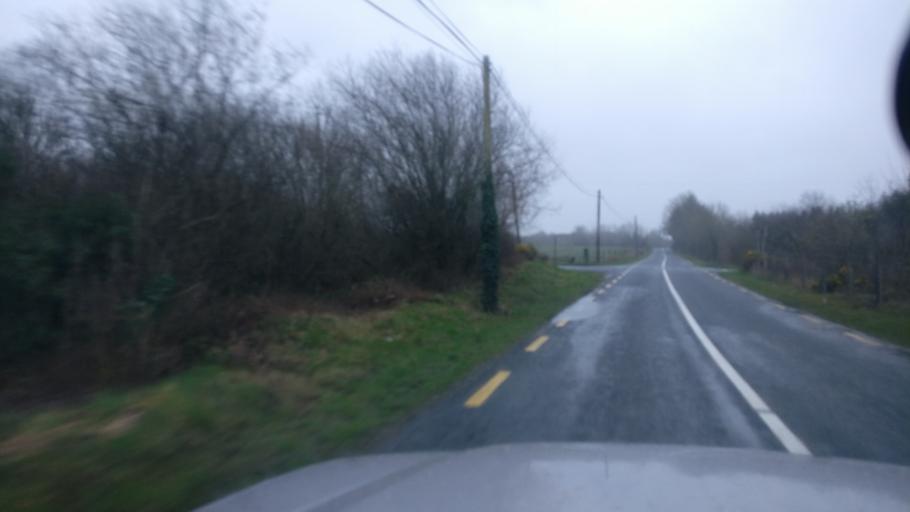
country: IE
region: Connaught
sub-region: County Galway
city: Ballinasloe
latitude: 53.2216
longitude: -8.1939
